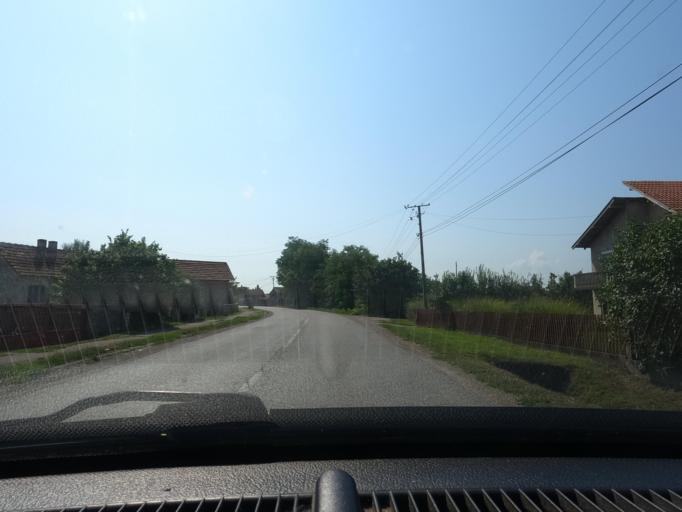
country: RS
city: Lipnicki Sor
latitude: 44.5819
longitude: 19.2584
